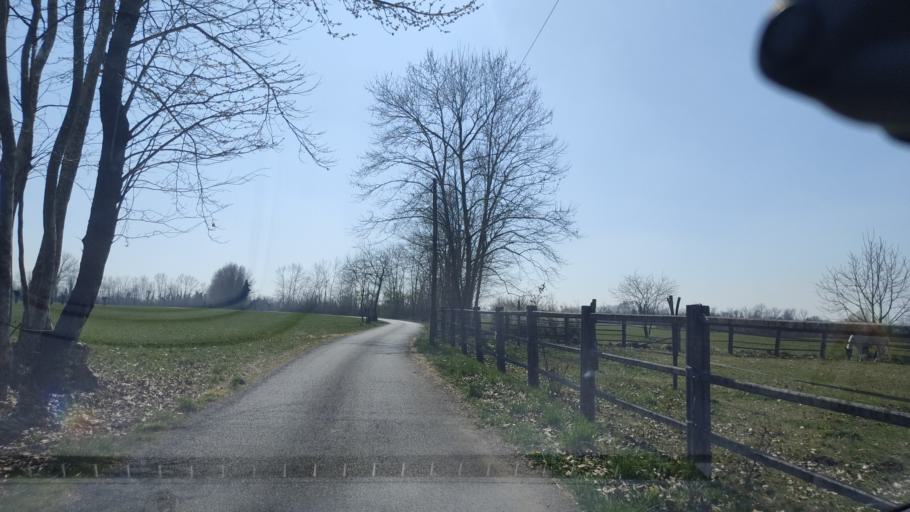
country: IT
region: Friuli Venezia Giulia
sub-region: Provincia di Pordenone
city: Budoia
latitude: 46.0280
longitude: 12.5347
